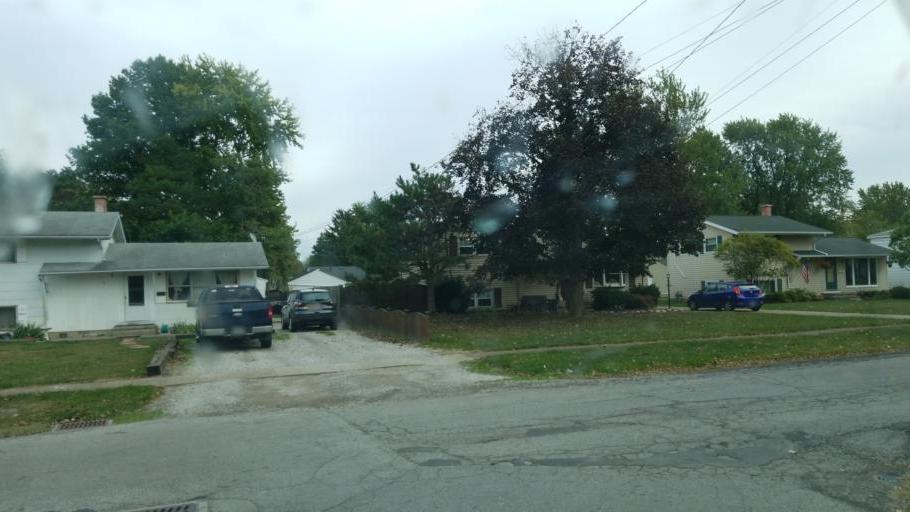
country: US
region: Ohio
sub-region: Lorain County
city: Sheffield Lake
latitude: 41.4826
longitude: -82.1198
